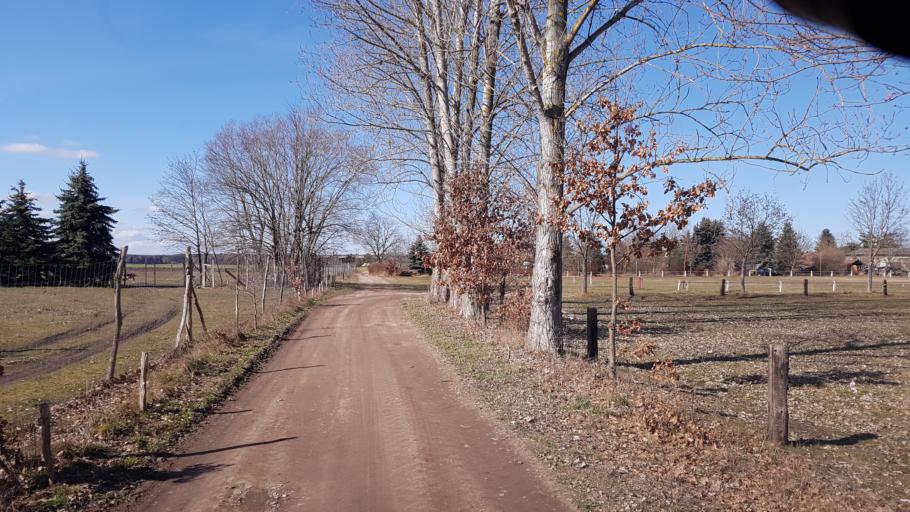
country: DE
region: Brandenburg
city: Schonborn
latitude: 51.5664
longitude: 13.5162
